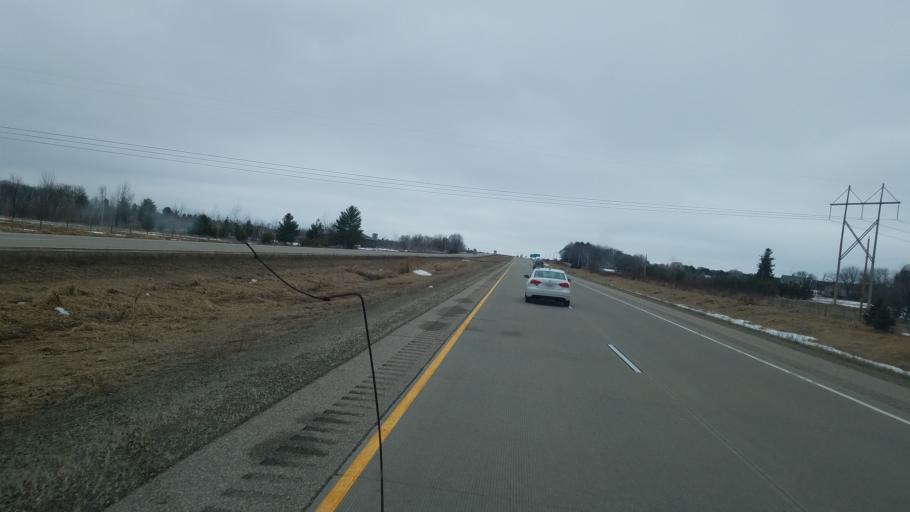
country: US
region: Wisconsin
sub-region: Portage County
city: Stevens Point
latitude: 44.5980
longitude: -89.7025
